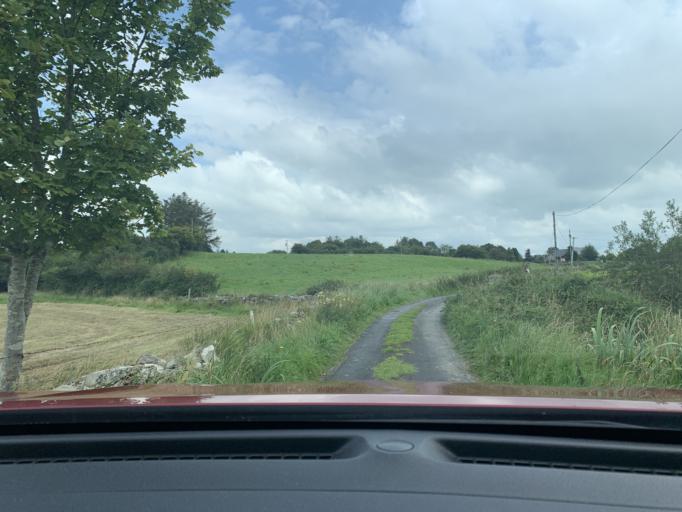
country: IE
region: Connaught
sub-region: Maigh Eo
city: Kiltamagh
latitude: 53.8415
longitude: -9.0057
